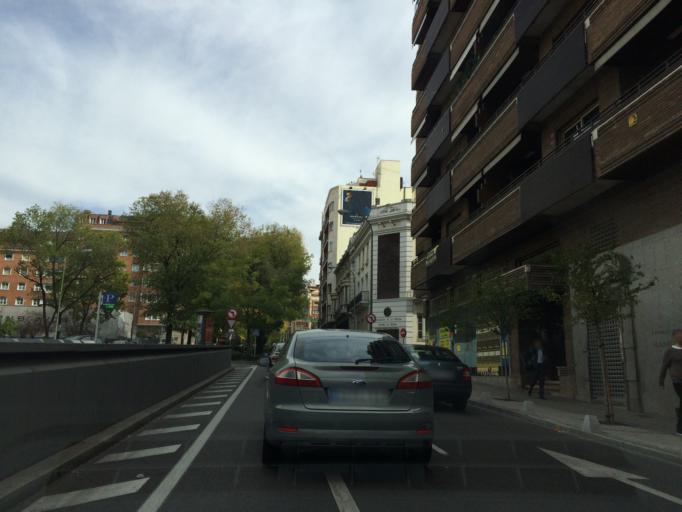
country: ES
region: Madrid
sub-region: Provincia de Madrid
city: Salamanca
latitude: 40.4329
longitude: -3.6861
